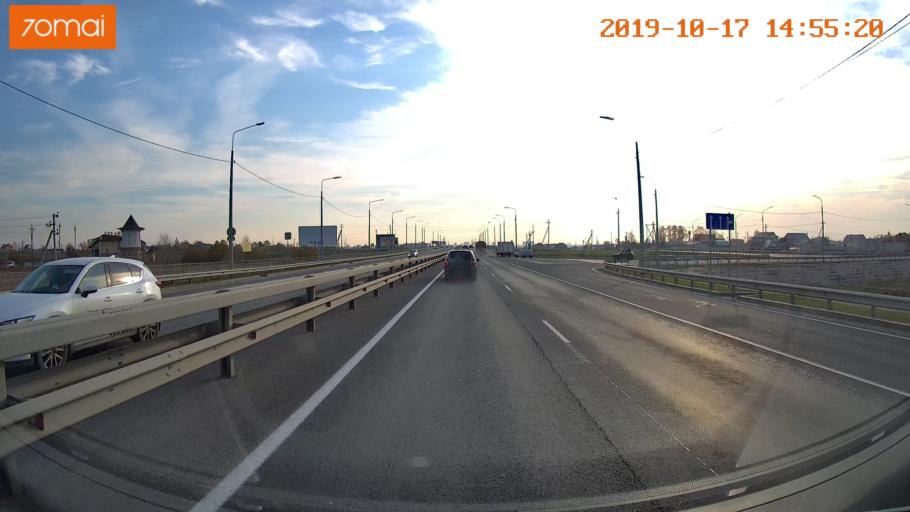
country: RU
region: Rjazan
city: Polyany
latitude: 54.6696
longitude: 39.8259
